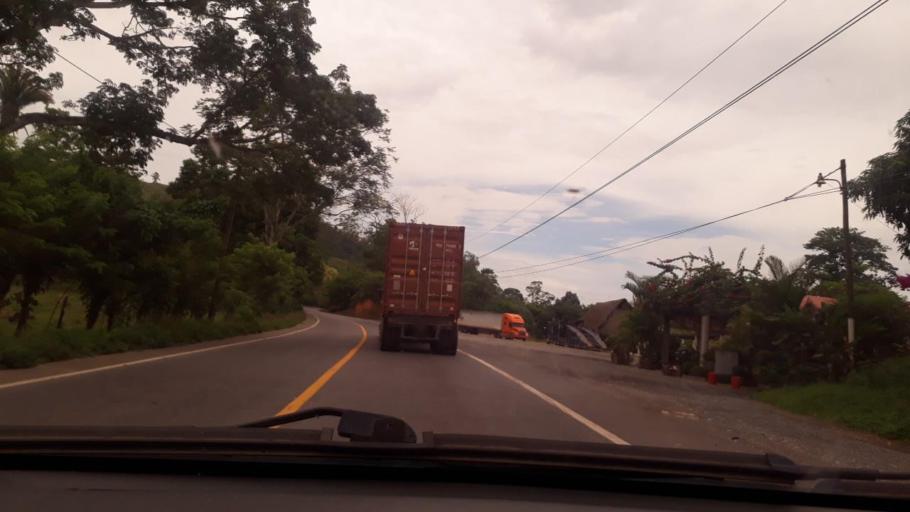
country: GT
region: Izabal
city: Morales
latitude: 15.5581
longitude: -88.6632
